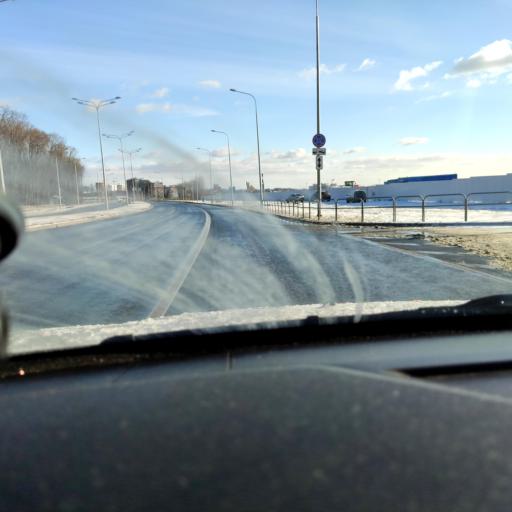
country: RU
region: Samara
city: Petra-Dubrava
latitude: 53.2800
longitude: 50.2464
